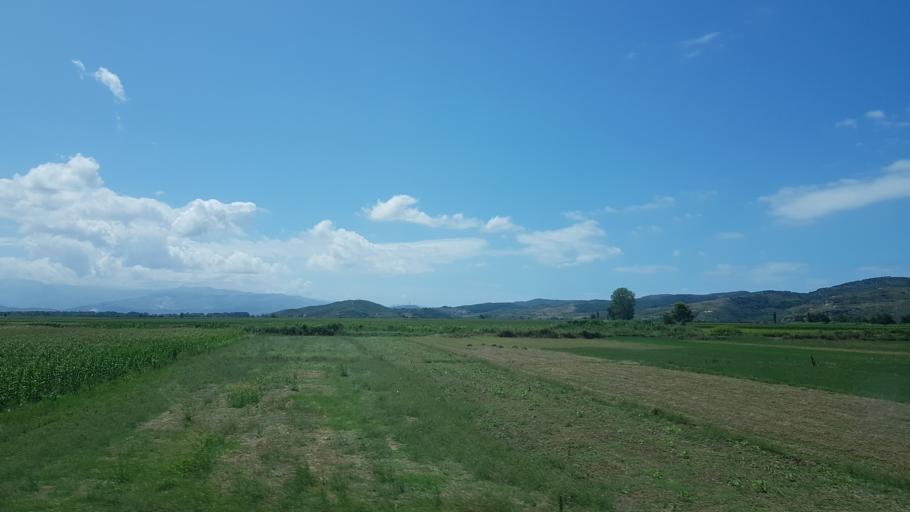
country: AL
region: Fier
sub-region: Rrethi i Fierit
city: Cakran
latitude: 40.6028
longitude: 19.5563
